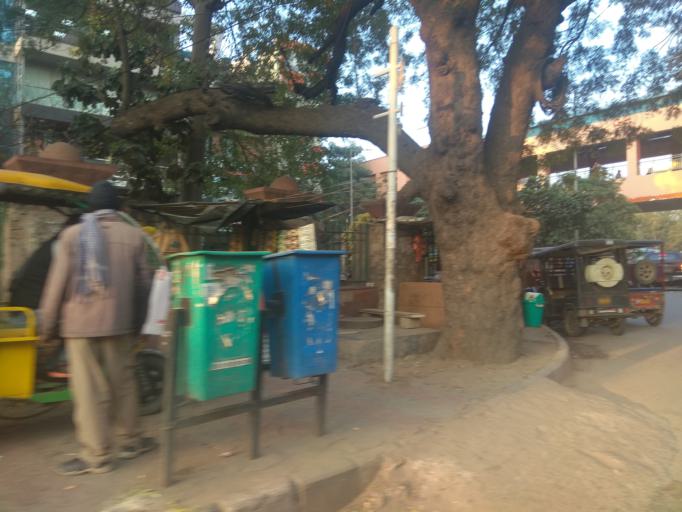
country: IN
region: NCT
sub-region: West Delhi
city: Nangloi Jat
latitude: 28.6296
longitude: 77.0771
